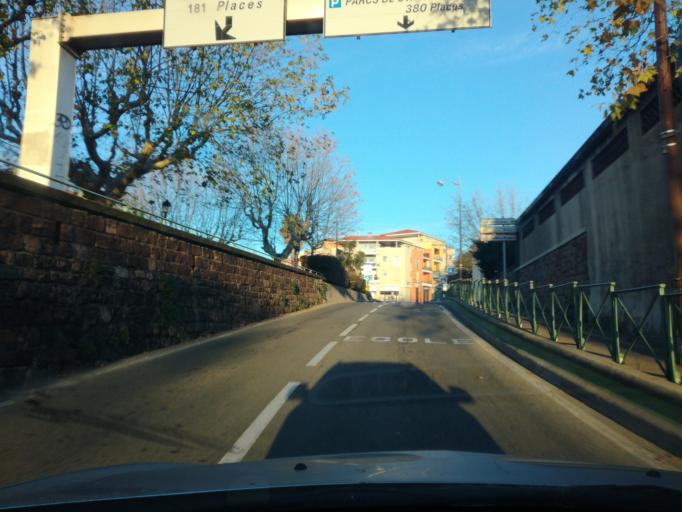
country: FR
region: Provence-Alpes-Cote d'Azur
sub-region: Departement du Var
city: Frejus
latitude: 43.4339
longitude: 6.7387
